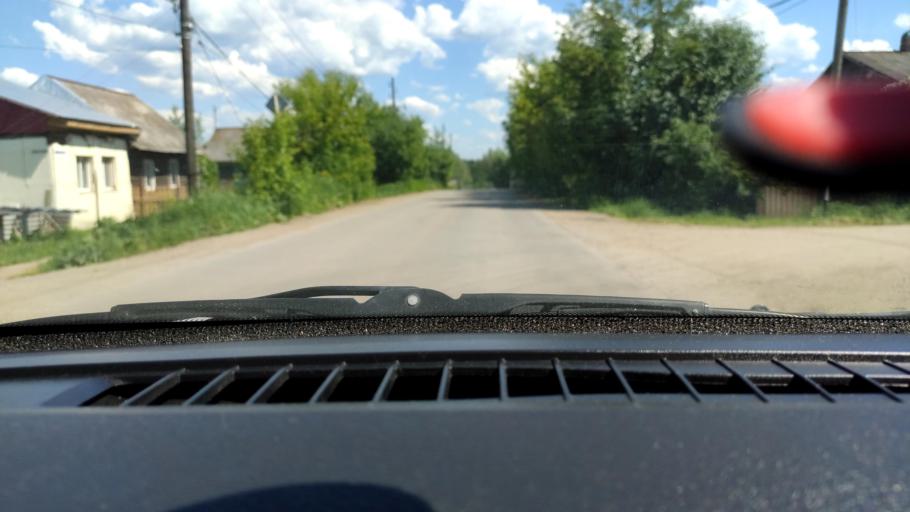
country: RU
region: Perm
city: Sylva
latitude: 58.0328
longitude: 56.7689
